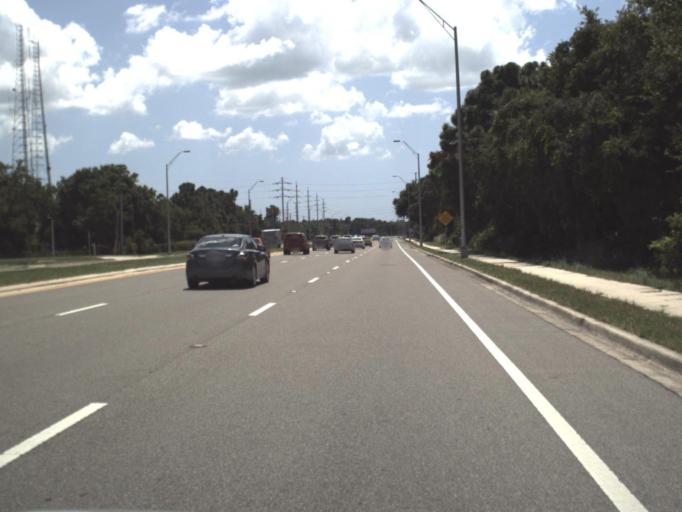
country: US
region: Florida
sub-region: Pinellas County
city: Ridgecrest
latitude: 27.8894
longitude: -82.8105
